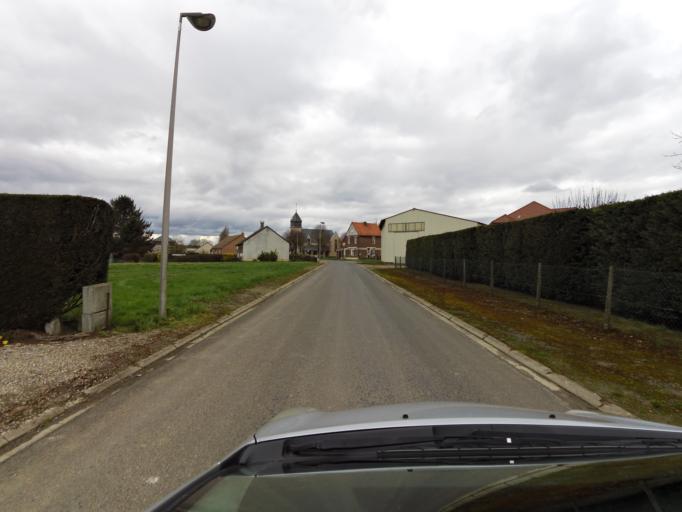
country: FR
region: Picardie
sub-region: Departement de la Somme
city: Chaulnes
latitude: 49.8847
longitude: 2.8091
